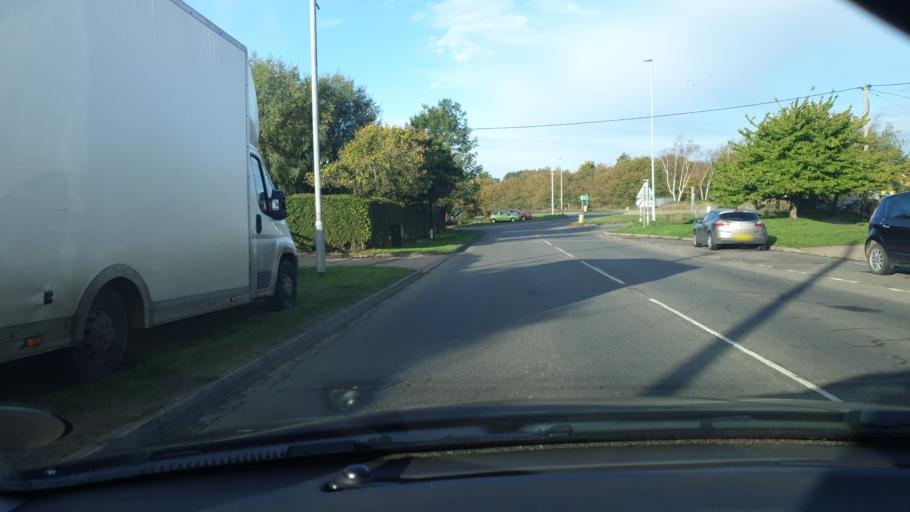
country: GB
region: England
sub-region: Suffolk
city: Shotley Gate
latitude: 51.9273
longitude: 1.2198
